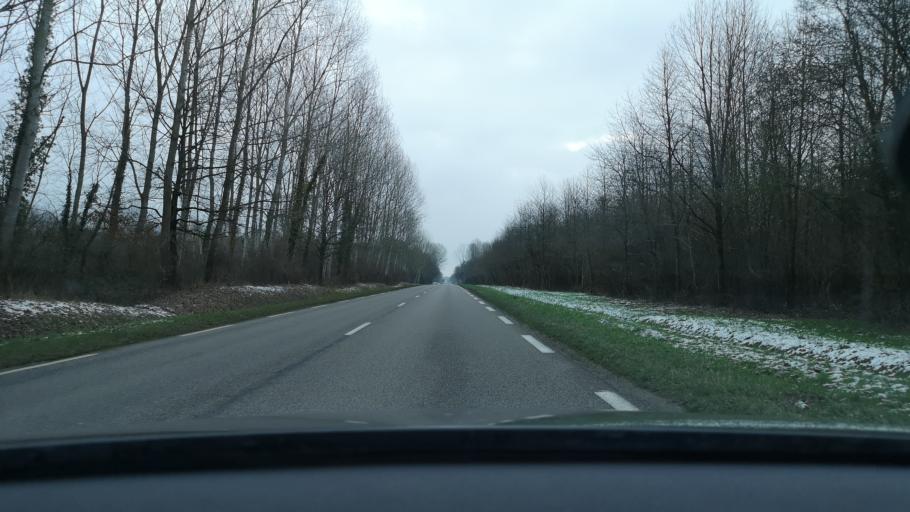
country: FR
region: Bourgogne
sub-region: Departement de Saone-et-Loire
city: Epervans
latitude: 46.7794
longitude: 4.9457
